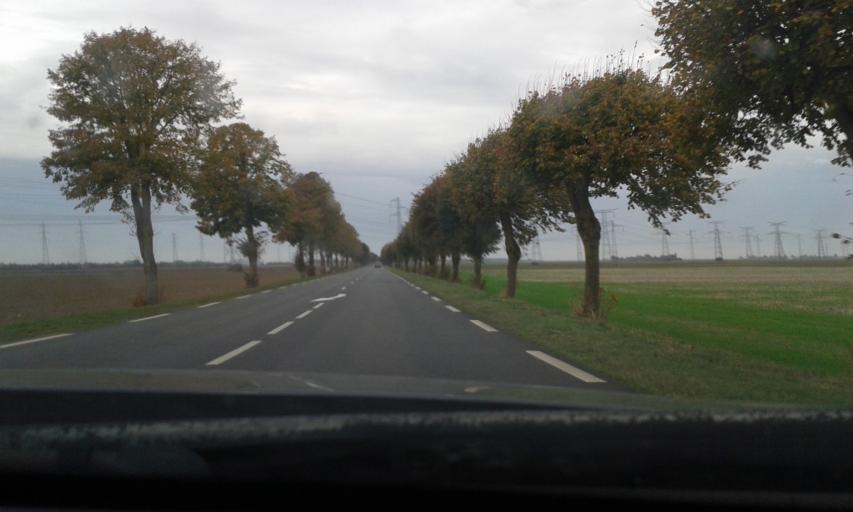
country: FR
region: Centre
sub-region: Departement du Loiret
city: Artenay
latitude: 48.1106
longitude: 1.8622
